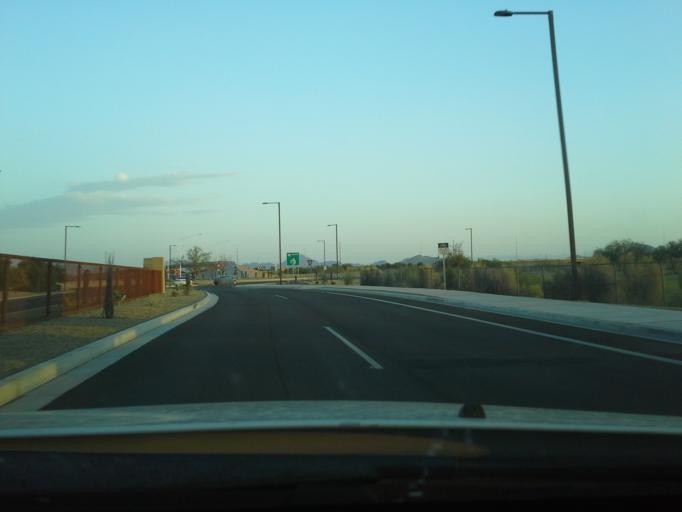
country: US
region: Arizona
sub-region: Maricopa County
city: Paradise Valley
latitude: 33.6777
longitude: -112.0051
